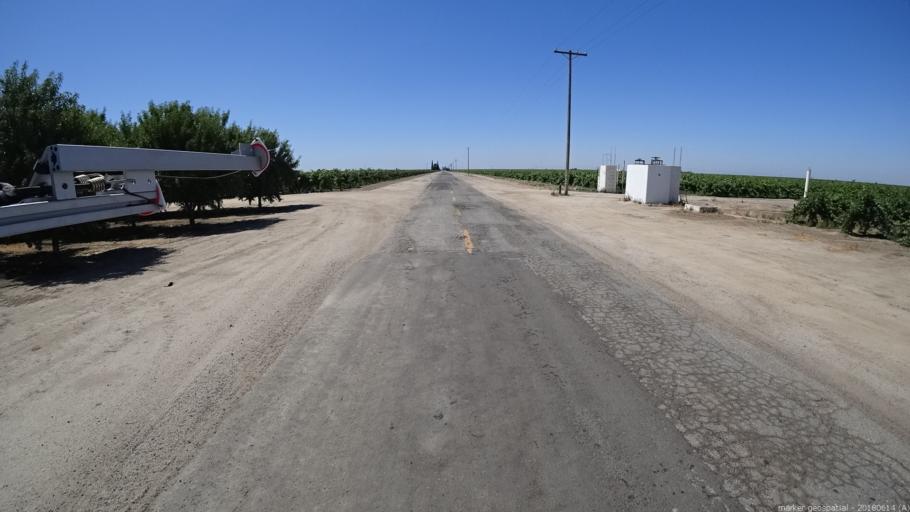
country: US
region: California
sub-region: Madera County
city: Fairmead
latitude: 36.9748
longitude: -120.1842
